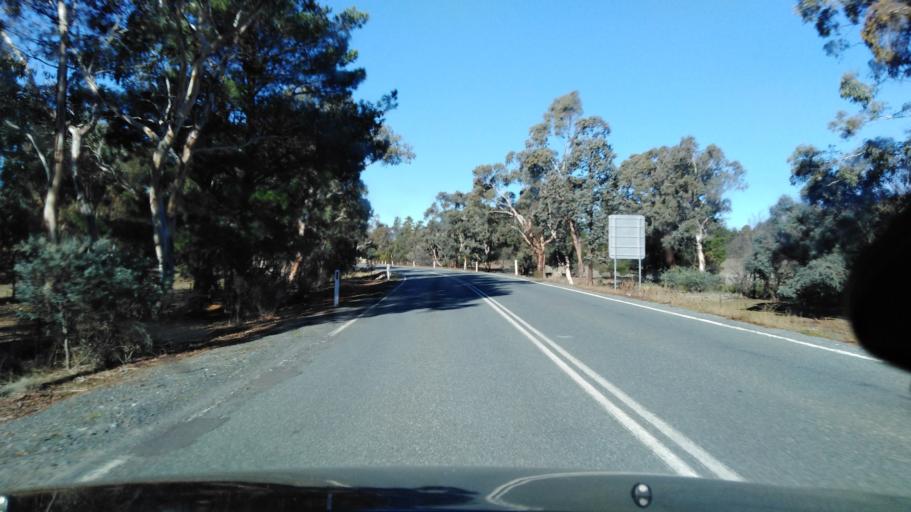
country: AU
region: New South Wales
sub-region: Palerang
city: Bungendore
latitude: -35.1902
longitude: 149.3313
